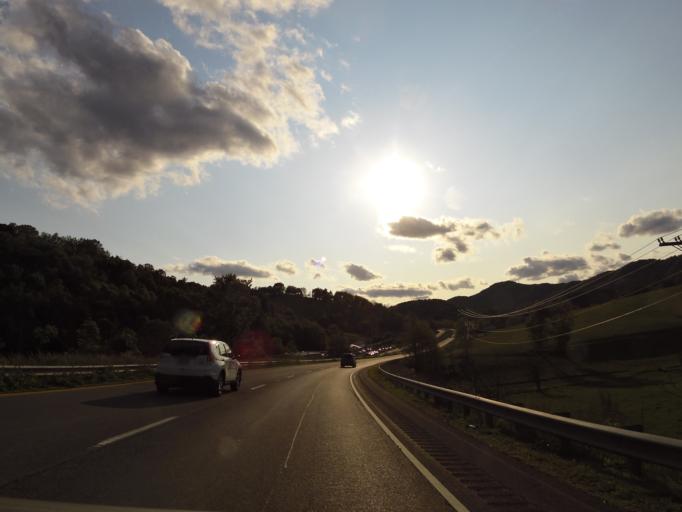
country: US
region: Virginia
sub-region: Russell County
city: Honaker
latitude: 36.9336
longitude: -81.9731
